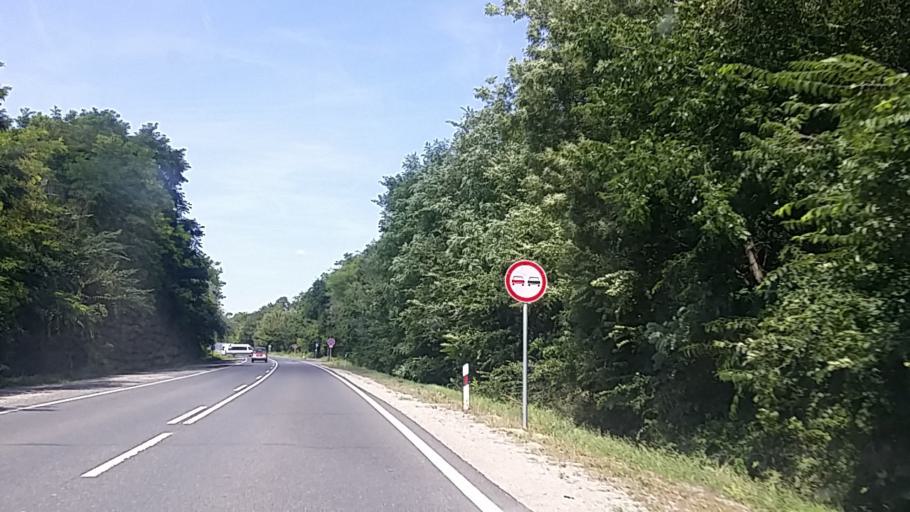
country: HU
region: Fejer
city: Deg
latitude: 46.8665
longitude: 18.4147
